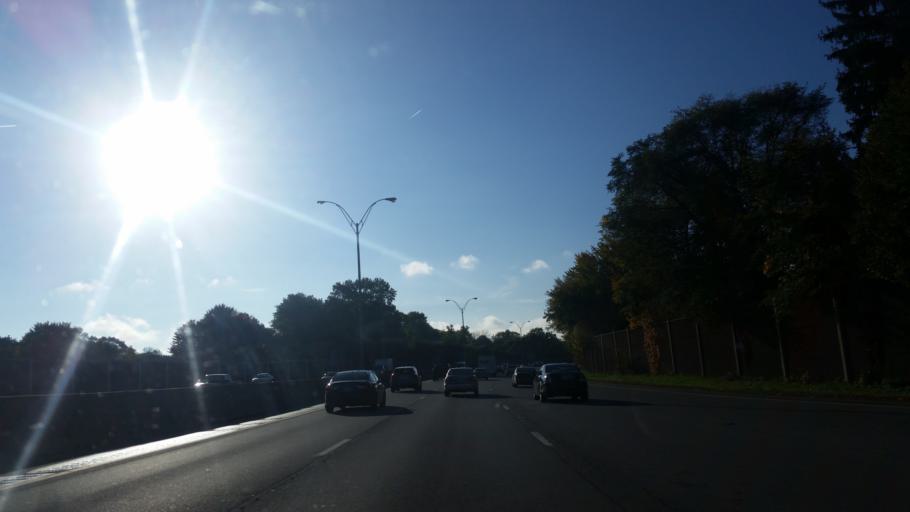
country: US
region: Ohio
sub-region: Summit County
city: Fairlawn
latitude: 41.0816
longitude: -81.5768
